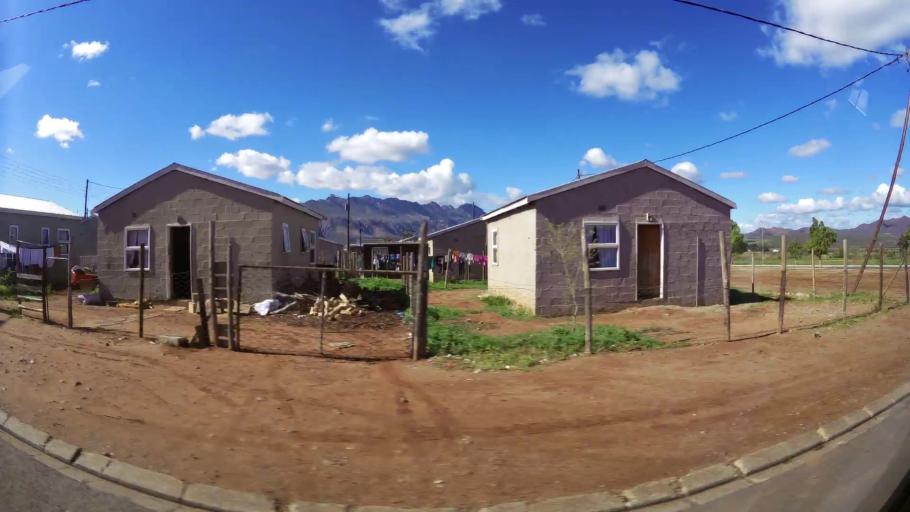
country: ZA
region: Western Cape
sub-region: Cape Winelands District Municipality
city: Ashton
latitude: -33.8355
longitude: 20.0434
